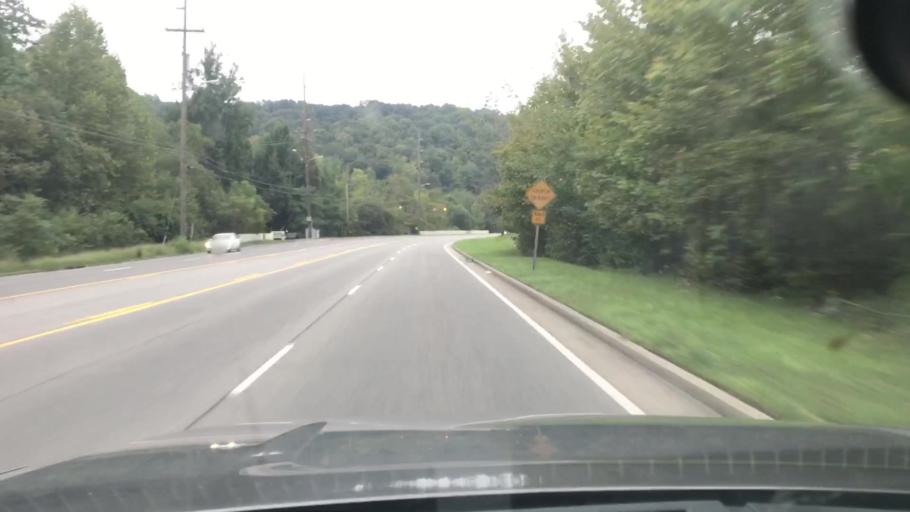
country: US
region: Tennessee
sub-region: Davidson County
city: Belle Meade
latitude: 36.0825
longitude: -86.9198
